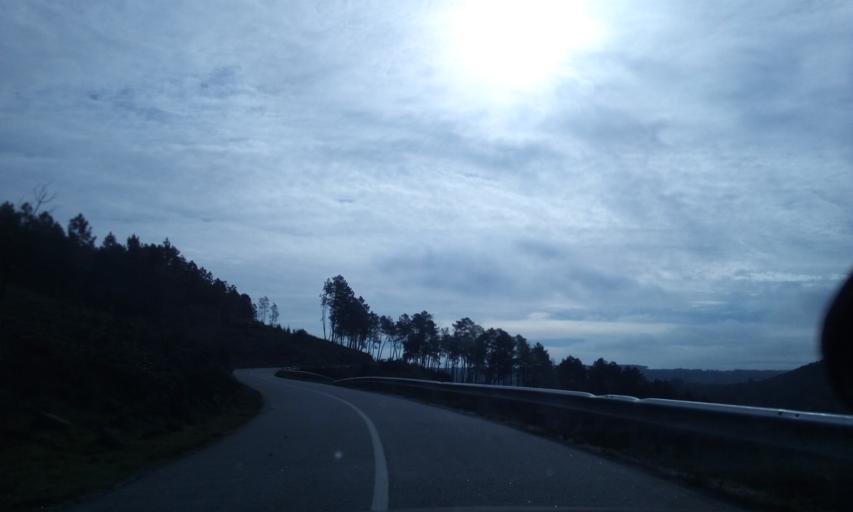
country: PT
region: Guarda
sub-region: Fornos de Algodres
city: Fornos de Algodres
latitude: 40.6863
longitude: -7.5399
